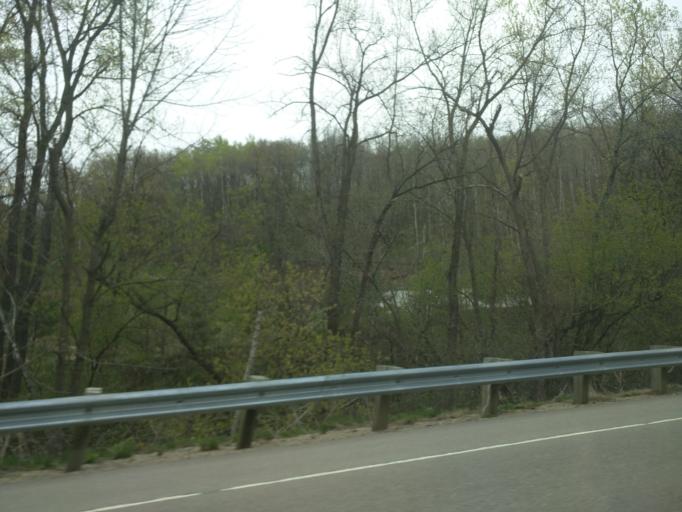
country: US
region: Minnesota
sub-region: Goodhue County
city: Red Wing
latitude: 44.5936
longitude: -92.4261
